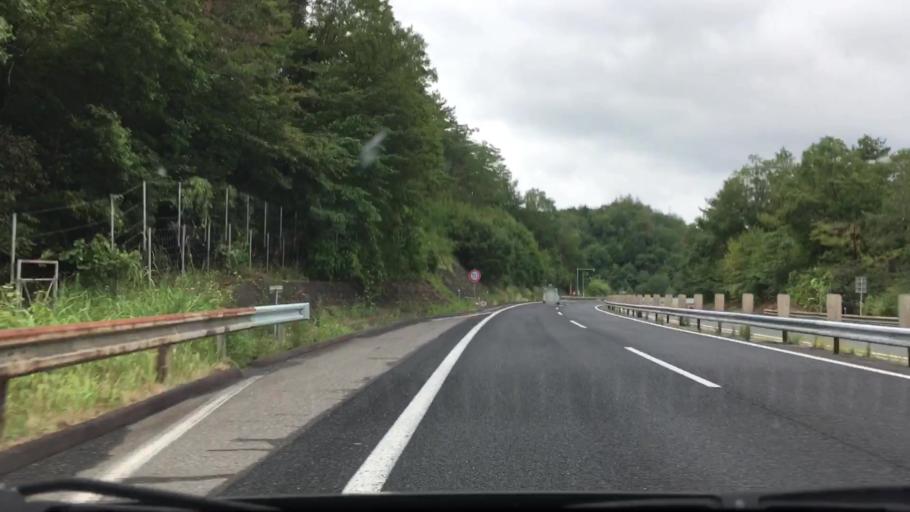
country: JP
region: Hiroshima
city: Miyoshi
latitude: 34.7367
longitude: 132.7115
